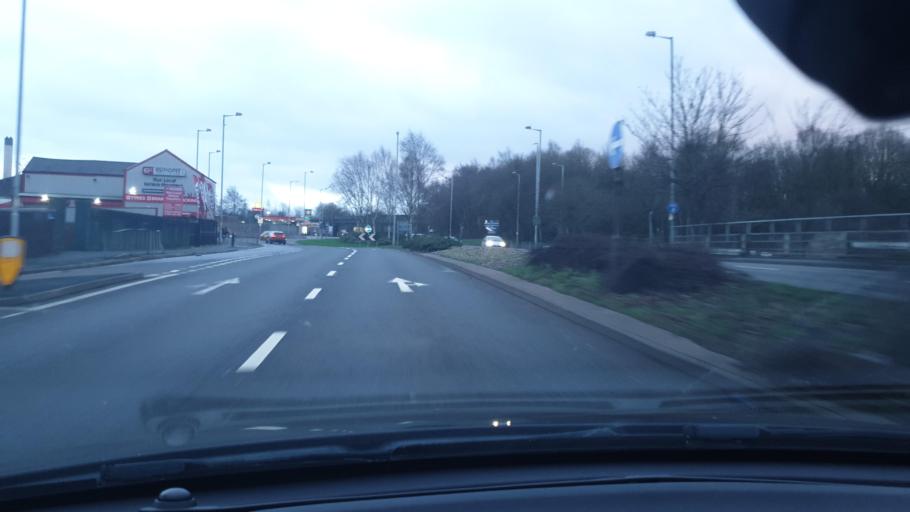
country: GB
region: England
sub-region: Wolverhampton
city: Wolverhampton
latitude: 52.6026
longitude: -2.1303
